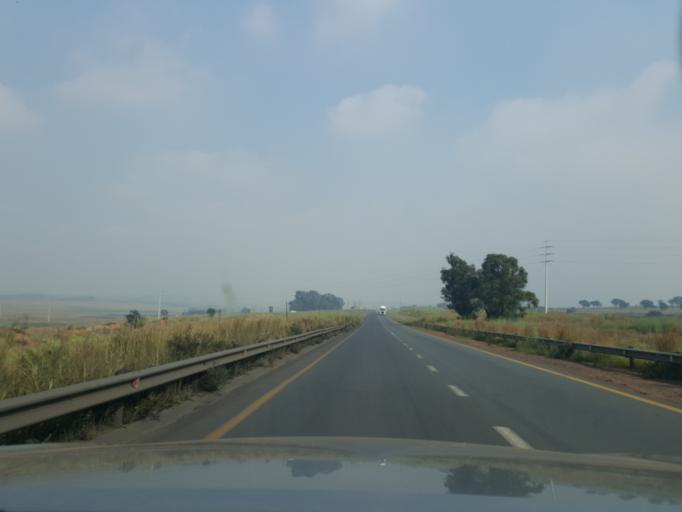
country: ZA
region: Mpumalanga
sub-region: Nkangala District Municipality
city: Witbank
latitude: -26.0154
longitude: 29.3079
